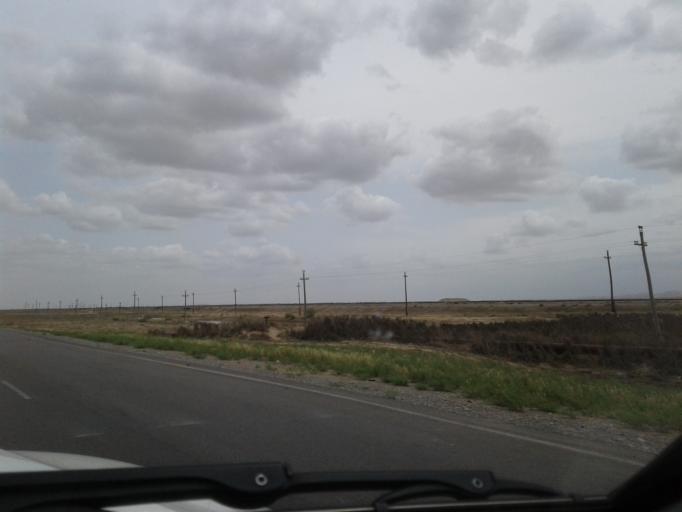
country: IR
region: Razavi Khorasan
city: Dargaz
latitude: 37.5912
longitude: 59.2414
